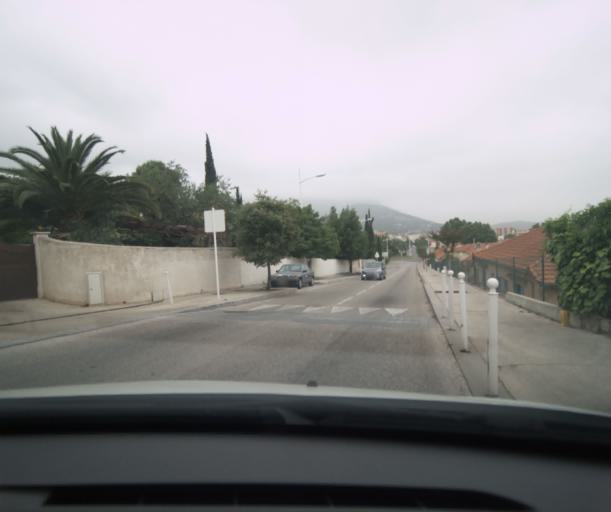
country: FR
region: Provence-Alpes-Cote d'Azur
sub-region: Departement du Var
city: La Valette-du-Var
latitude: 43.1344
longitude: 5.9761
